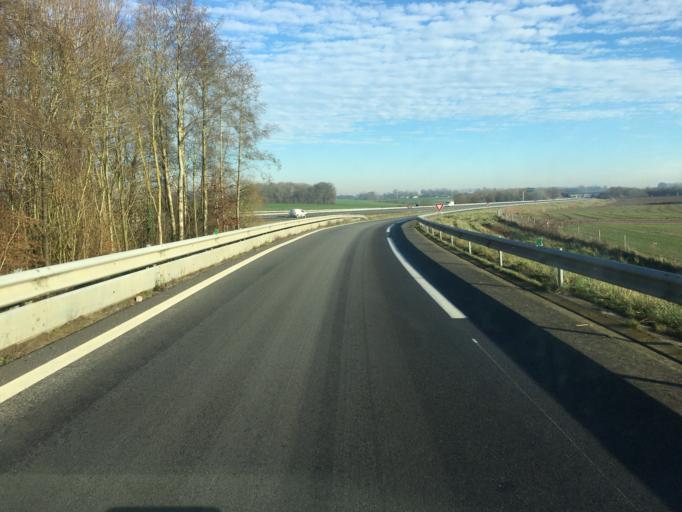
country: FR
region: Haute-Normandie
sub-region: Departement de la Seine-Maritime
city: Yerville
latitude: 49.6514
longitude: 0.8463
